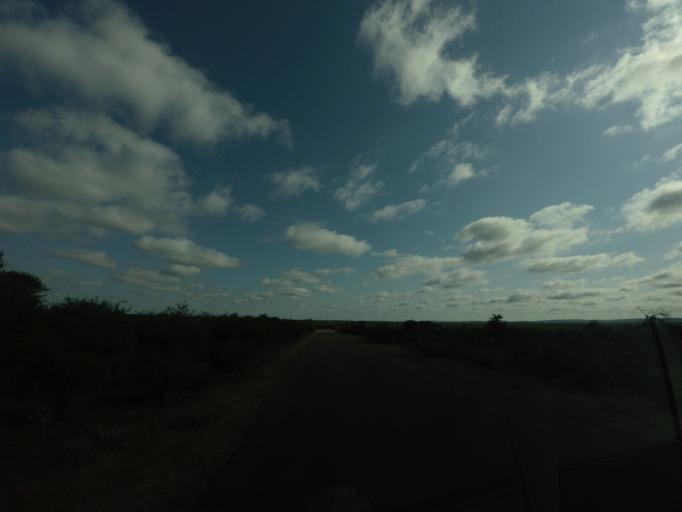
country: ZA
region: Mpumalanga
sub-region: Ehlanzeni District
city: Komatipoort
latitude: -25.1614
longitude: 31.9308
